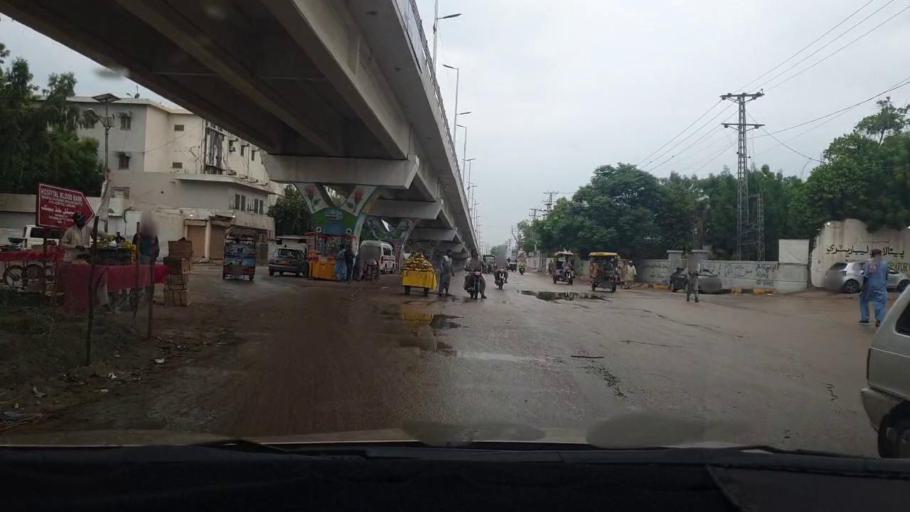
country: PK
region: Sindh
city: Larkana
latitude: 27.5616
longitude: 68.2063
